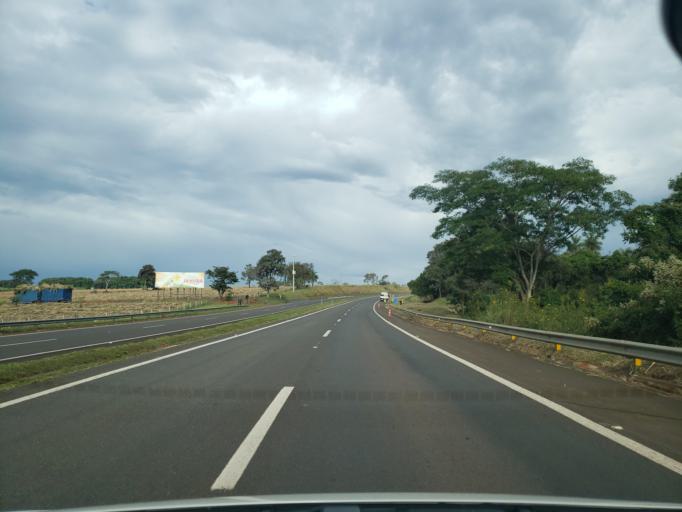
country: BR
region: Sao Paulo
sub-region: Dois Corregos
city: Dois Corregos
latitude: -22.2556
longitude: -48.3643
